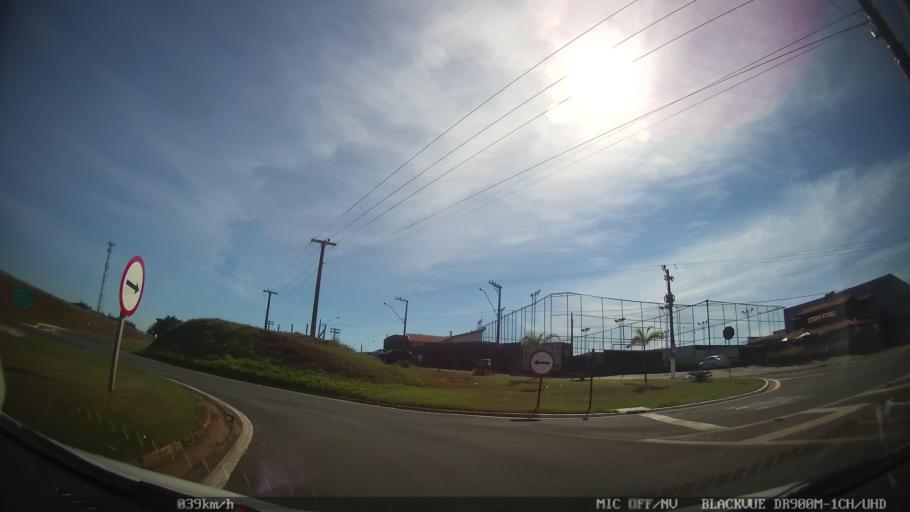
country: BR
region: Sao Paulo
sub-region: Pirassununga
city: Pirassununga
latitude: -22.0132
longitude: -47.4400
